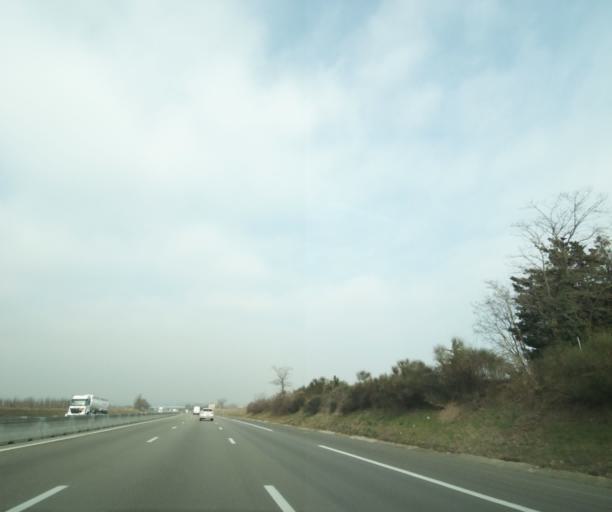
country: FR
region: Rhone-Alpes
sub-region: Departement de la Drome
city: Mercurol
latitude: 45.0432
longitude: 4.8784
